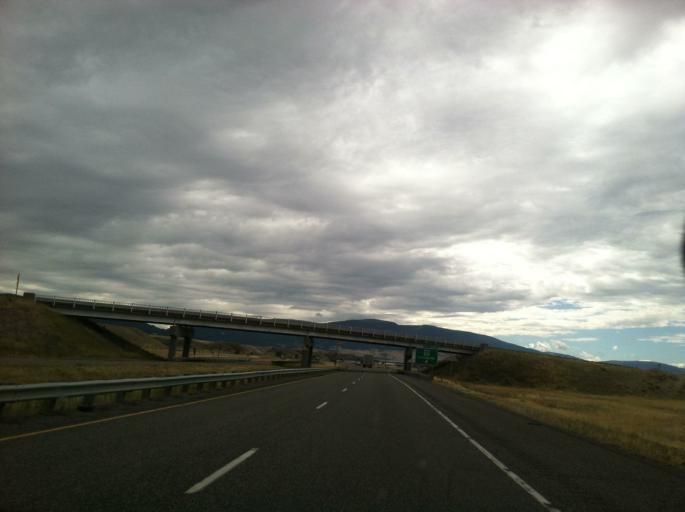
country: US
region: Montana
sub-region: Park County
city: Livingston
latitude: 45.6885
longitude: -110.4998
